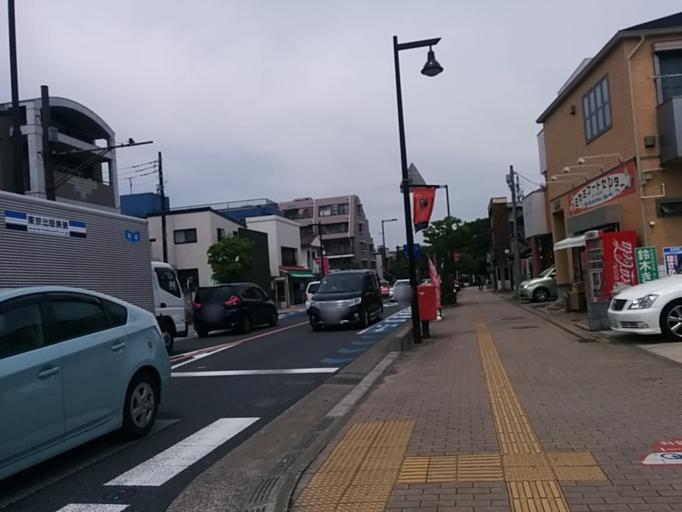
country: JP
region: Saitama
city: Shiki
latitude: 35.8334
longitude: 139.5793
